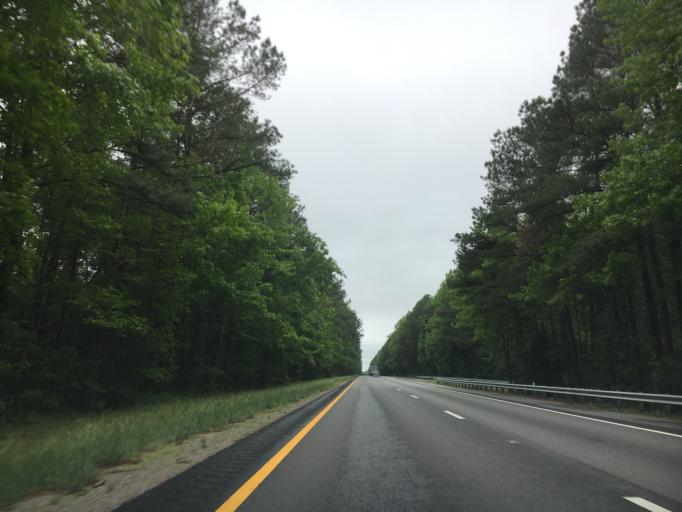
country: US
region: Virginia
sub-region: Dinwiddie County
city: Dinwiddie
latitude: 37.0351
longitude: -77.6321
